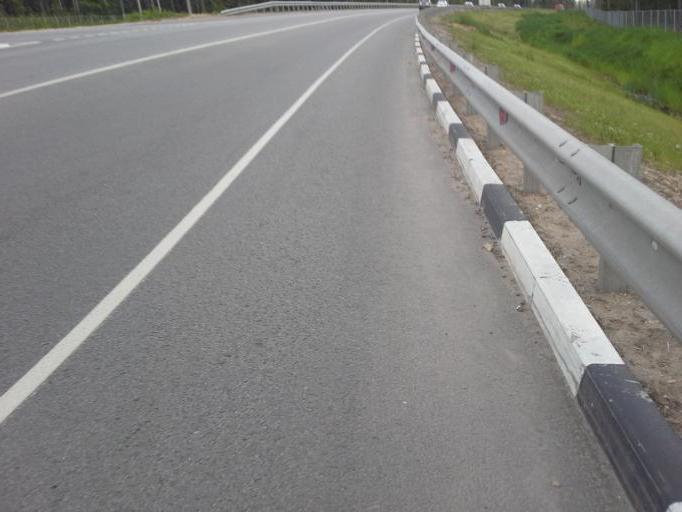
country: RU
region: Moskovskaya
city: Gorki Vtoryye
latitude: 55.6787
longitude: 37.1645
